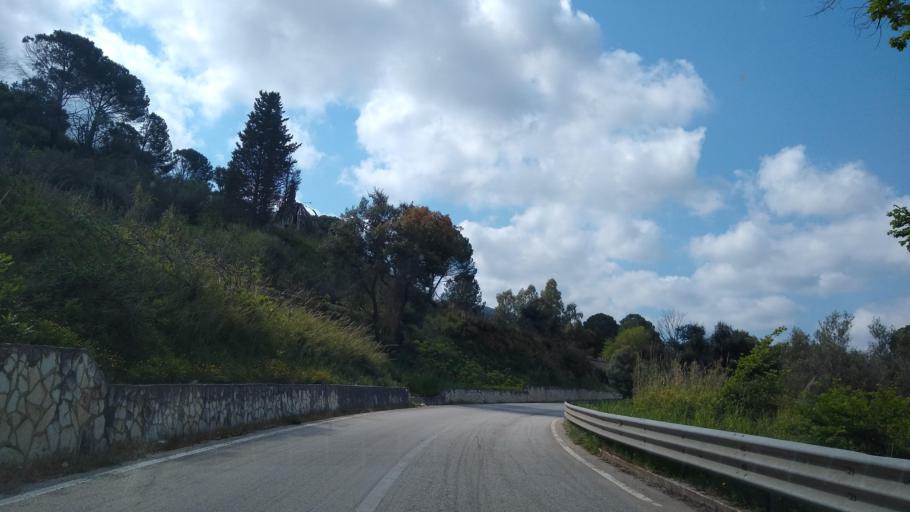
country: IT
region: Sicily
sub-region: Trapani
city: Calatafimi
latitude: 37.9463
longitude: 12.8614
